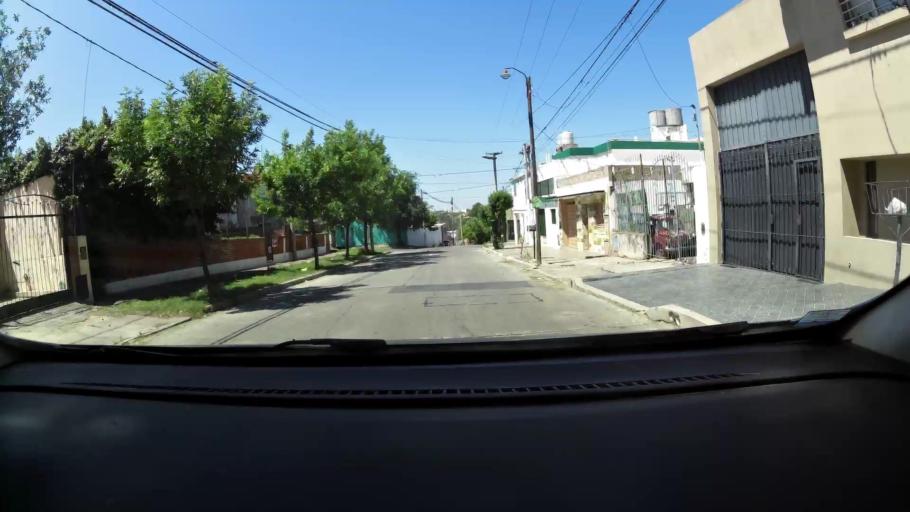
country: AR
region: Cordoba
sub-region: Departamento de Capital
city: Cordoba
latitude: -31.4292
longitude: -64.2065
